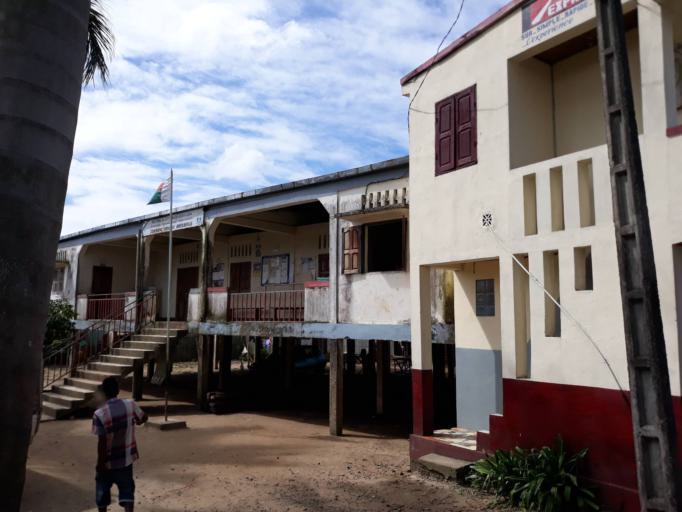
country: MG
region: Atsinanana
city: Ampasimanolotra
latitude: -18.8211
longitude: 49.0694
